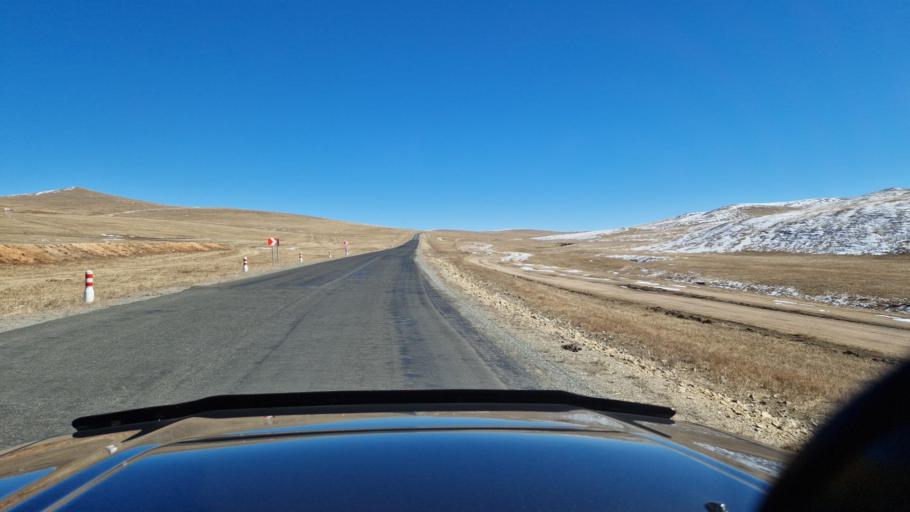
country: MN
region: Hentiy
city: Modot
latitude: 47.8042
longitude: 108.7059
